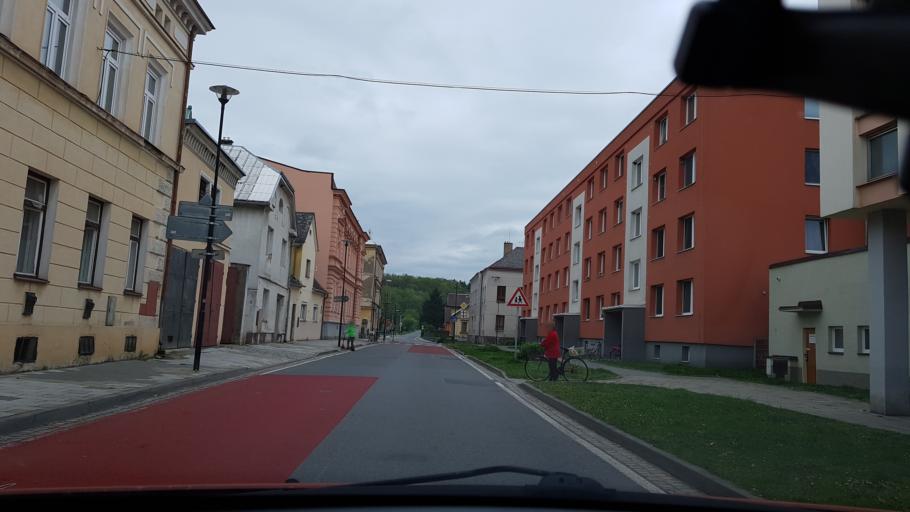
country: CZ
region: Olomoucky
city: Vidnava
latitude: 50.3723
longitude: 17.1864
